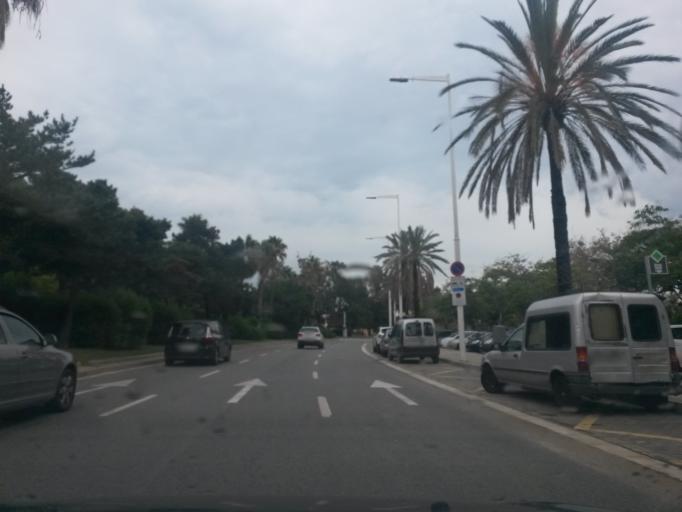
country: ES
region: Catalonia
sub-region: Provincia de Barcelona
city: Sant Marti
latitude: 41.3903
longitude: 2.2003
